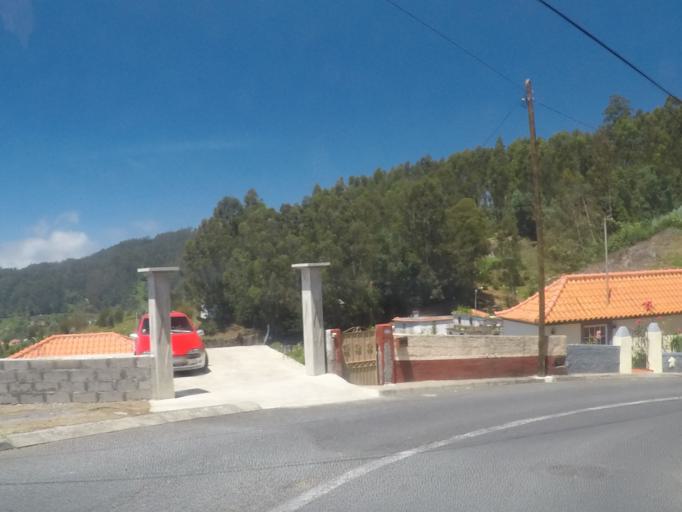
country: PT
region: Madeira
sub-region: Camara de Lobos
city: Curral das Freiras
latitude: 32.6865
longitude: -16.9841
